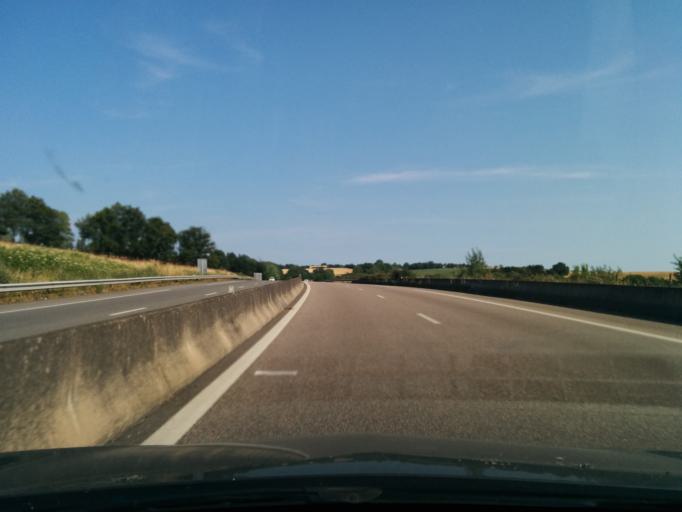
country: FR
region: Limousin
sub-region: Departement de la Haute-Vienne
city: Pierre-Buffiere
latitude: 45.7273
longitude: 1.3425
